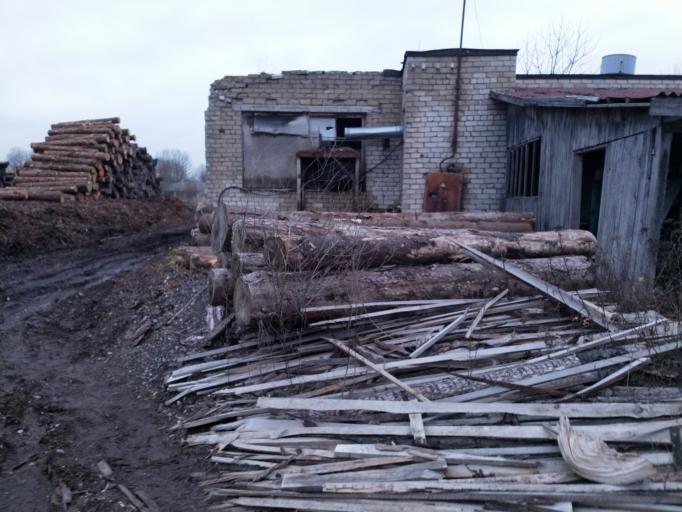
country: LV
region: Alsunga
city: Alsunga
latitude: 57.0253
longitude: 21.6735
